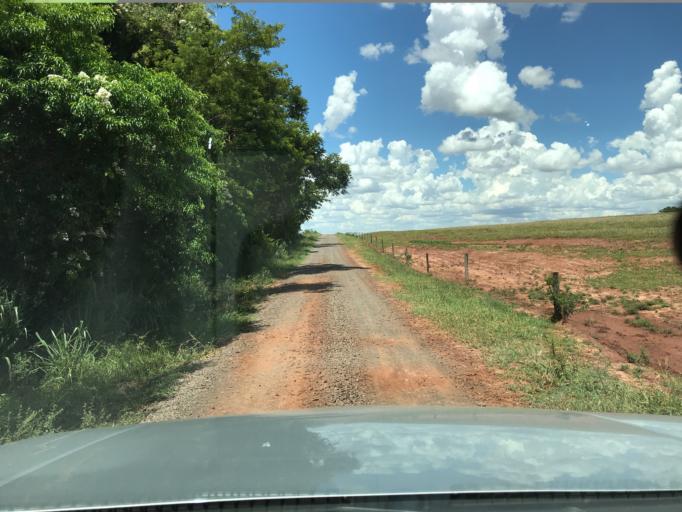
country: BR
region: Parana
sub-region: Palotina
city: Palotina
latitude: -24.1783
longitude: -53.7769
